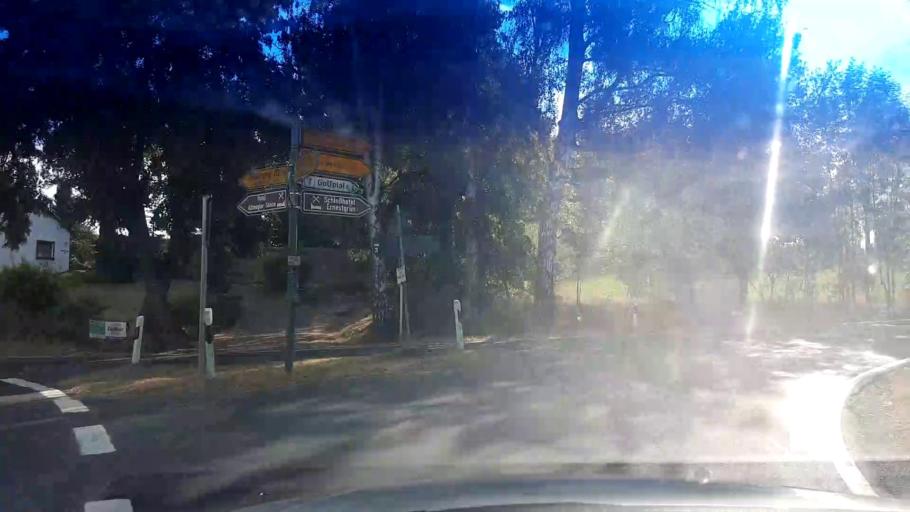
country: DE
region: Bavaria
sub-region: Upper Palatinate
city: Neualbenreuth
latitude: 49.9702
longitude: 12.4440
